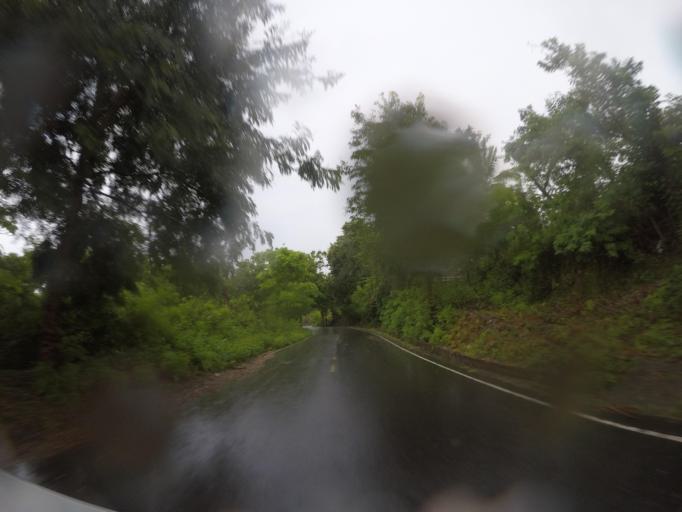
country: TL
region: Bobonaro
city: Maliana
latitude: -8.9537
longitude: 125.0690
